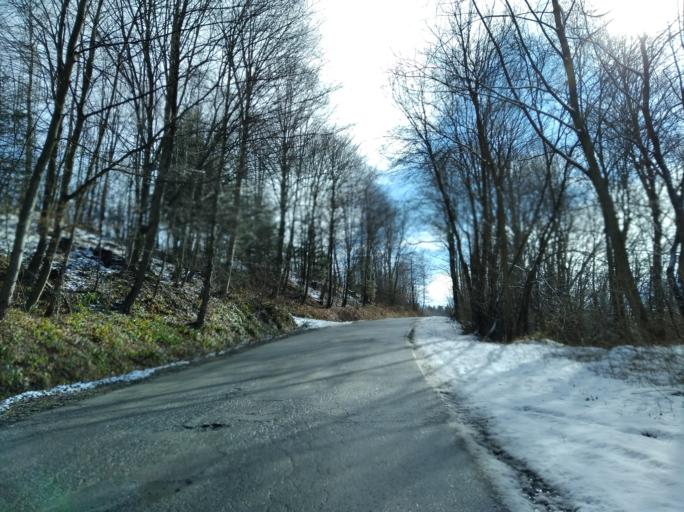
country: PL
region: Subcarpathian Voivodeship
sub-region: Powiat brzozowski
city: Jablonica Polska
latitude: 49.7321
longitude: 21.8945
